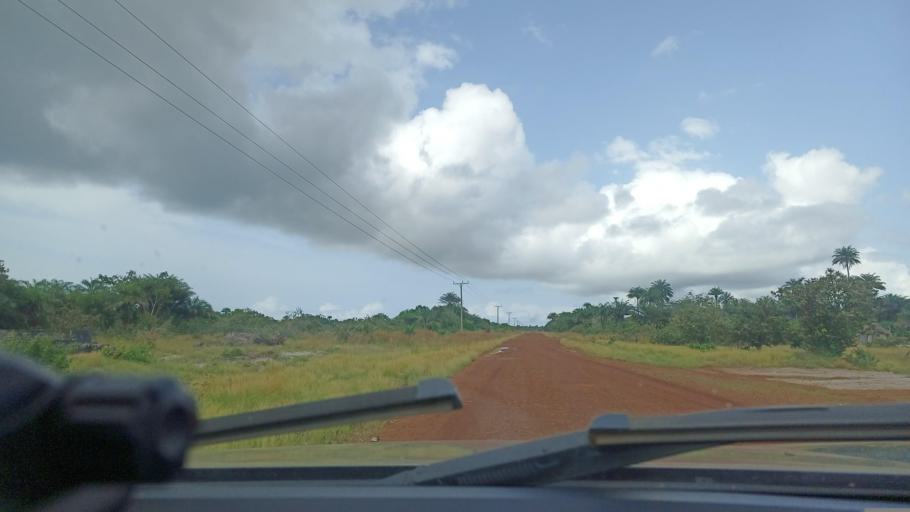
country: LR
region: Grand Cape Mount
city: Robertsport
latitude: 6.6914
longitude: -11.2686
